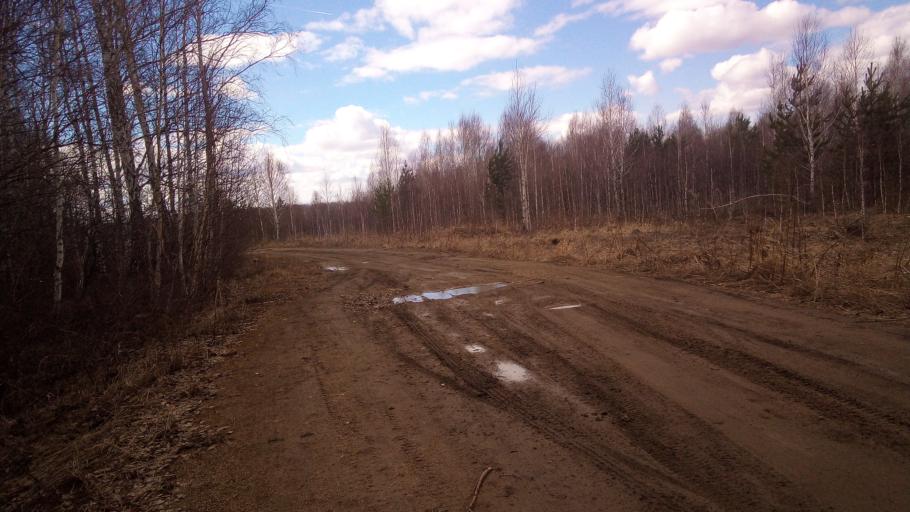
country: RU
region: Chelyabinsk
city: Sargazy
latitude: 55.1226
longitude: 61.2507
